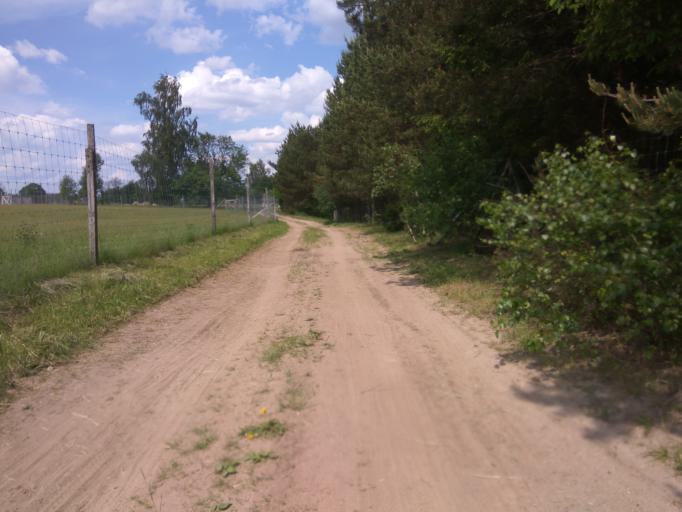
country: LV
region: Kuldigas Rajons
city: Kuldiga
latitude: 56.8882
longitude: 21.9300
